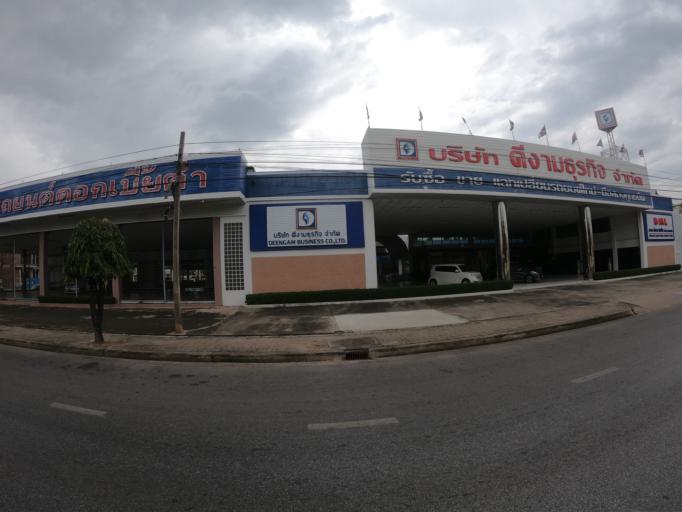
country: TH
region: Roi Et
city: Roi Et
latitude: 16.0534
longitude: 103.6456
